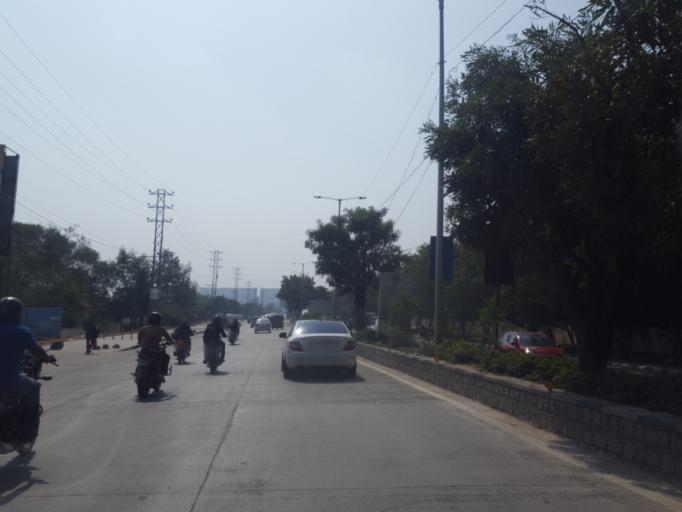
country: IN
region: Telangana
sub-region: Medak
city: Serilingampalle
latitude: 17.4358
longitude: 78.3468
